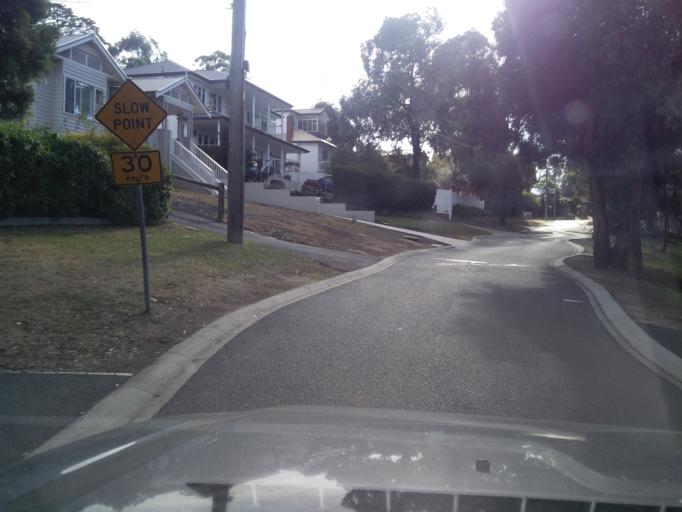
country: AU
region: Victoria
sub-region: Nillumbik
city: Eltham
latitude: -37.7233
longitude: 145.1610
